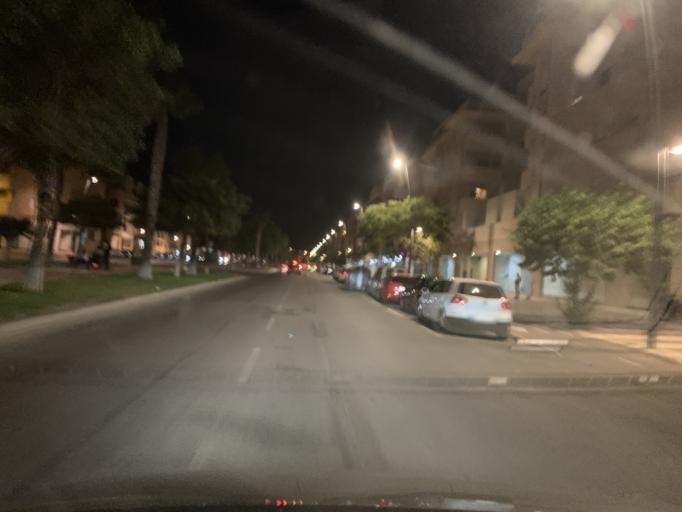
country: ES
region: Andalusia
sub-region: Provincia de Almeria
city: Roquetas de Mar
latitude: 36.7746
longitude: -2.6090
